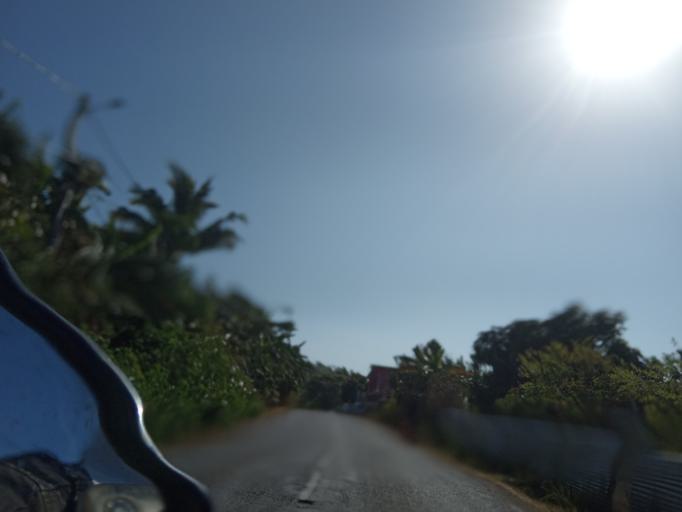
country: YT
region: Bandrele
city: Bandrele
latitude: -12.8951
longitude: 45.1993
